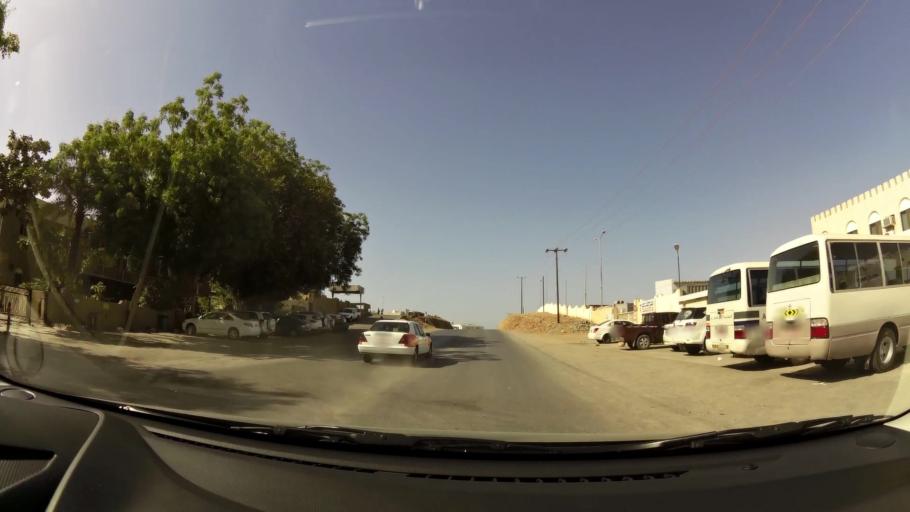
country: OM
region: Muhafazat Masqat
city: Bawshar
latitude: 23.5777
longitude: 58.3616
